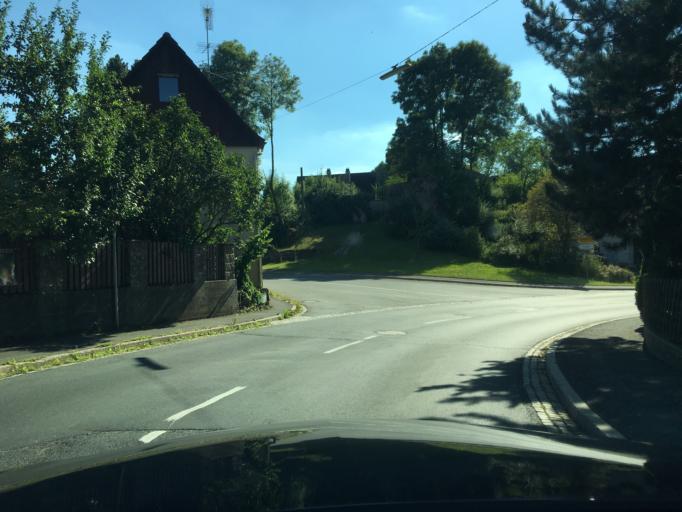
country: DE
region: Bavaria
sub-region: Upper Franconia
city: Hiltpoltstein
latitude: 49.6600
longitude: 11.3199
